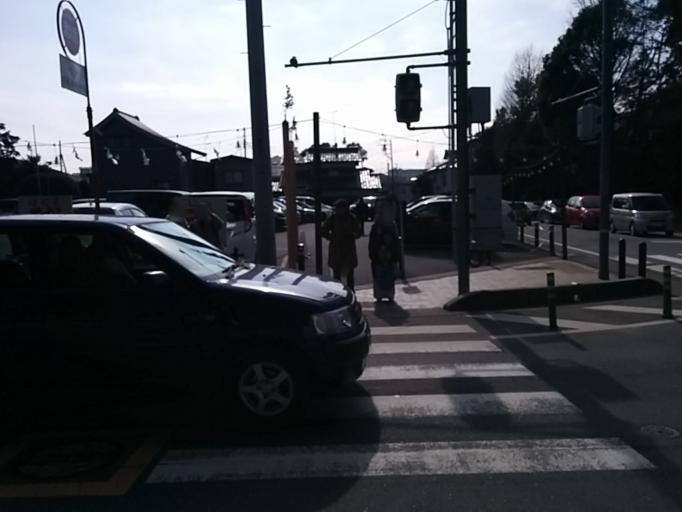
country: JP
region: Saitama
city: Kawagoe
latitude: 35.9273
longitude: 139.4886
